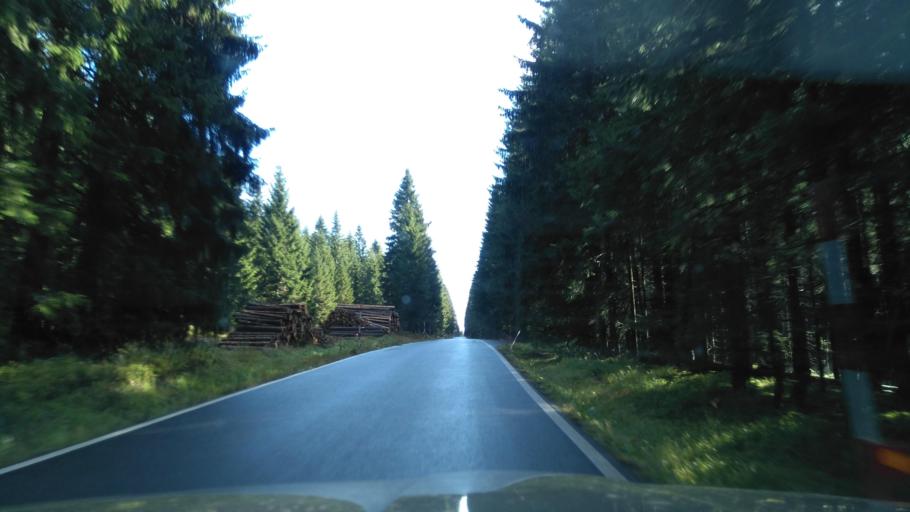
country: CZ
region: Plzensky
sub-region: Okres Klatovy
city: Kasperske Hory
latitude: 49.0276
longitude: 13.5380
